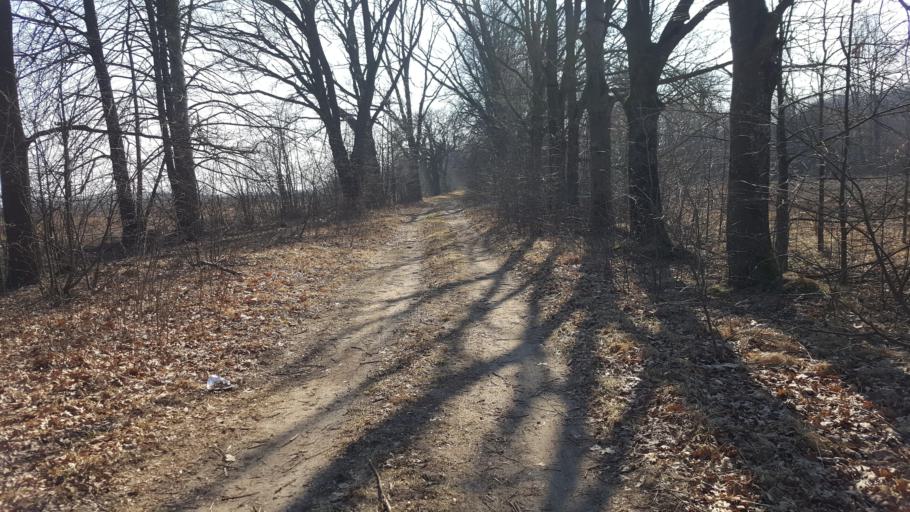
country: BY
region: Brest
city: Zhabinka
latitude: 52.3171
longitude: 23.9304
